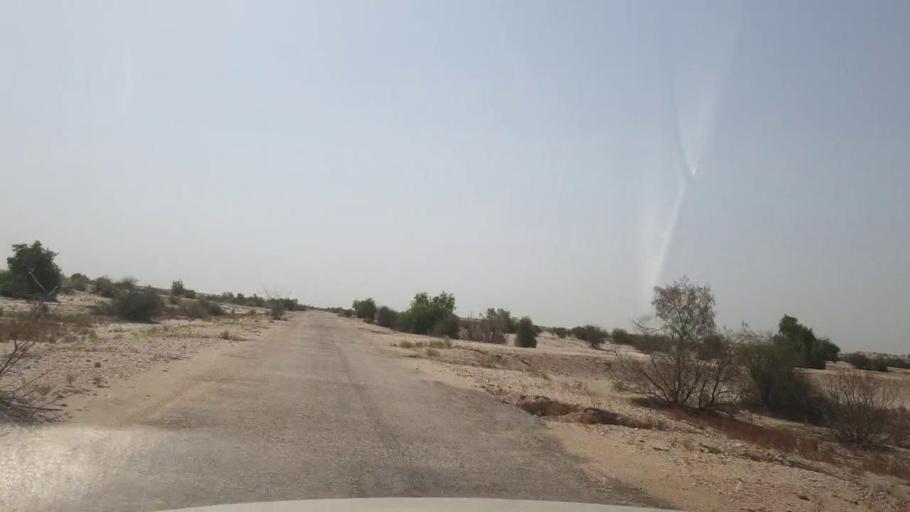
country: PK
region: Sindh
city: Rohri
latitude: 27.4489
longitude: 69.2315
